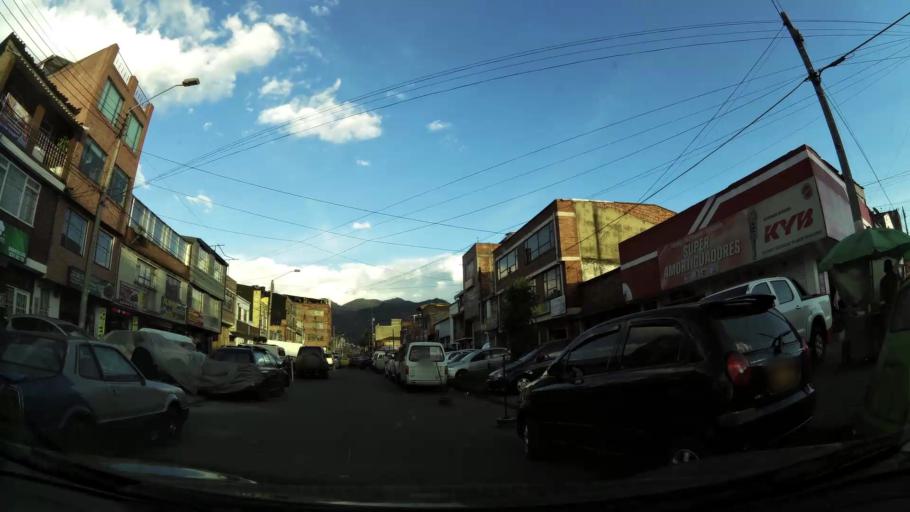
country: CO
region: Bogota D.C.
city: Bogota
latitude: 4.6580
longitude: -74.0759
